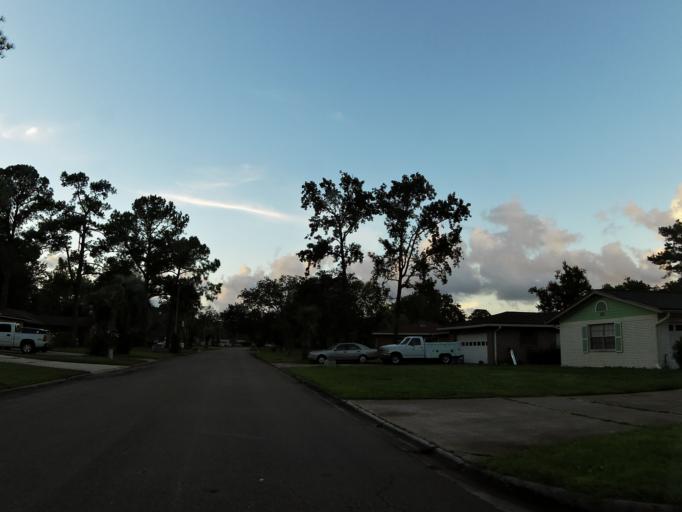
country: US
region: Florida
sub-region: Duval County
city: Jacksonville
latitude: 30.2367
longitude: -81.6043
